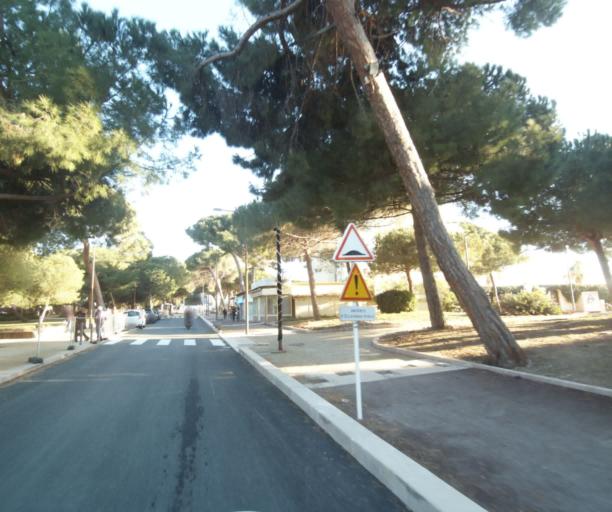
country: FR
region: Provence-Alpes-Cote d'Azur
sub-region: Departement des Alpes-Maritimes
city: Antibes
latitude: 43.5671
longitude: 7.1143
